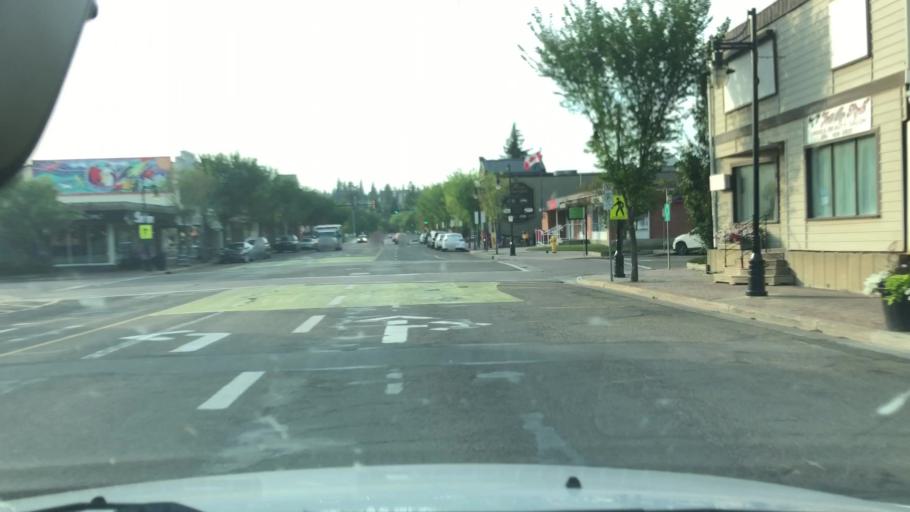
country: CA
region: Alberta
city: St. Albert
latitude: 53.6336
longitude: -113.6249
